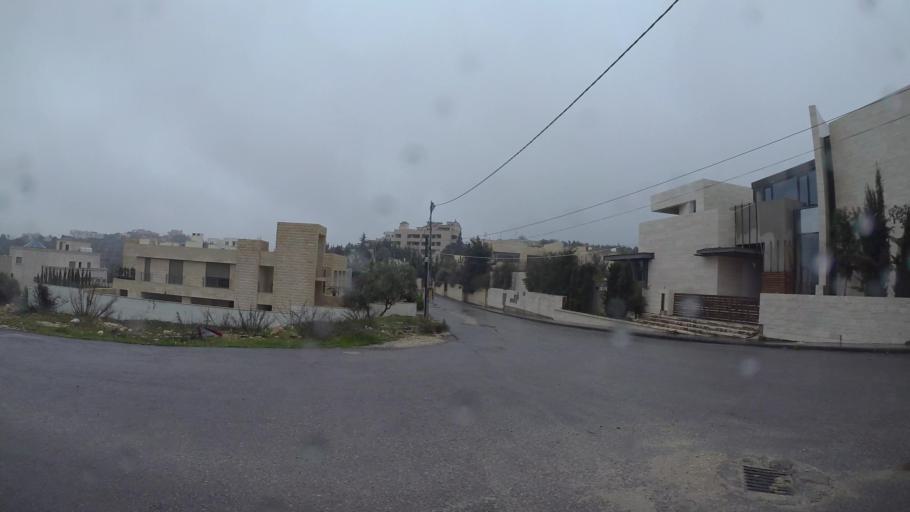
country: JO
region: Amman
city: Wadi as Sir
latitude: 32.0049
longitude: 35.7995
